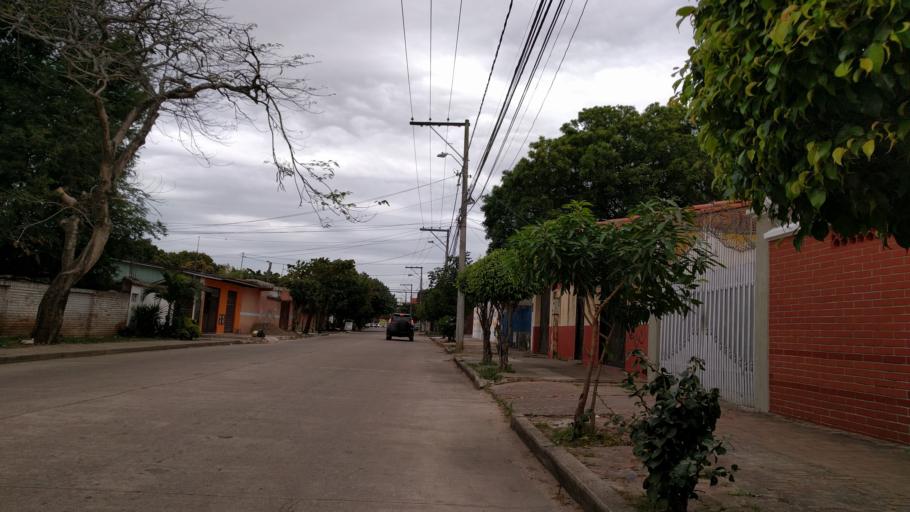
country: BO
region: Santa Cruz
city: Santa Cruz de la Sierra
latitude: -17.7927
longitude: -63.2134
